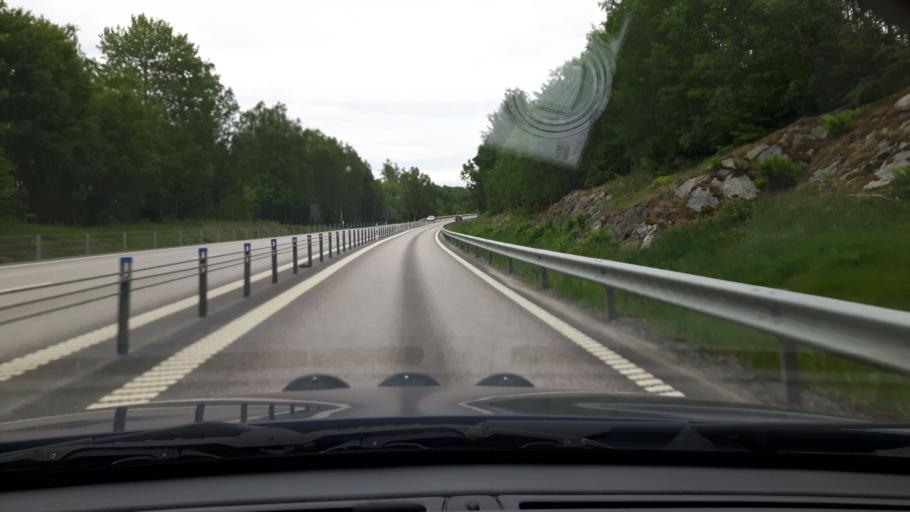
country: SE
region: Soedermanland
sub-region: Flens Kommun
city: Flen
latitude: 59.0415
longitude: 16.5122
